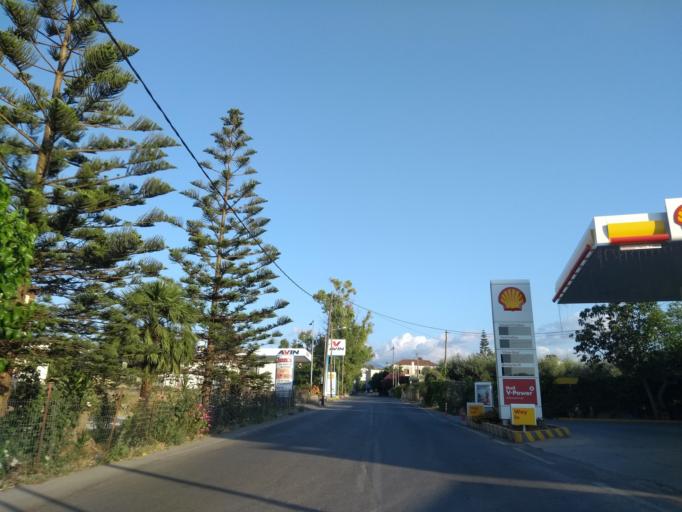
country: GR
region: Crete
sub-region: Nomos Chanias
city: Kalivai
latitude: 35.4118
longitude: 24.1958
